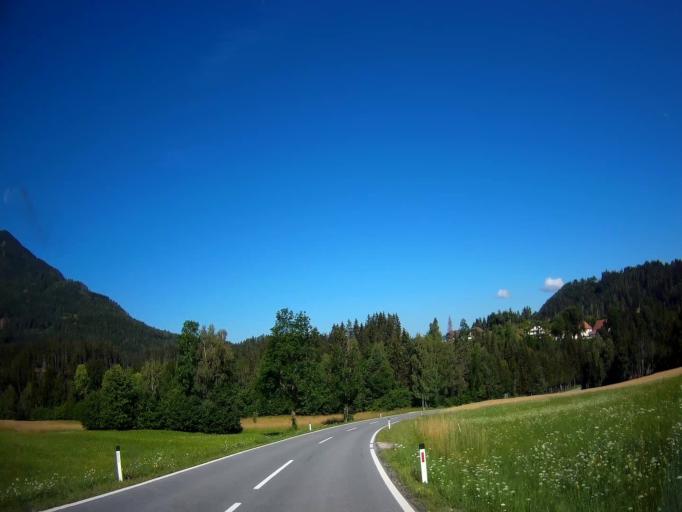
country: AT
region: Carinthia
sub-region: Politischer Bezirk Volkermarkt
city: Gallizien
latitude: 46.5331
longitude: 14.4595
